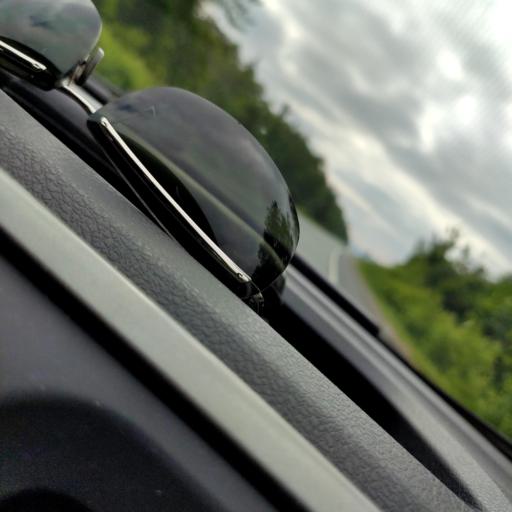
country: RU
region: Samara
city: Pribrezhnyy
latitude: 53.5103
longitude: 49.9295
